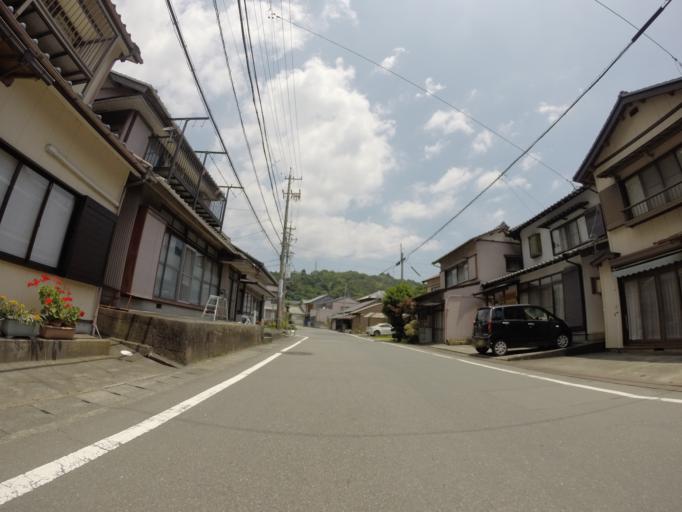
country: JP
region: Shizuoka
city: Kanaya
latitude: 34.8000
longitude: 138.0751
